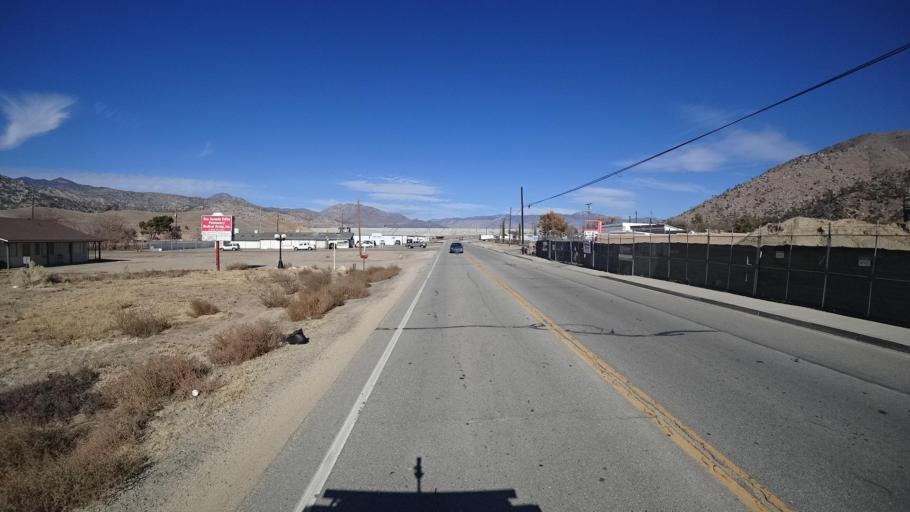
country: US
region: California
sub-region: Kern County
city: Lake Isabella
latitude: 35.6326
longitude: -118.4724
